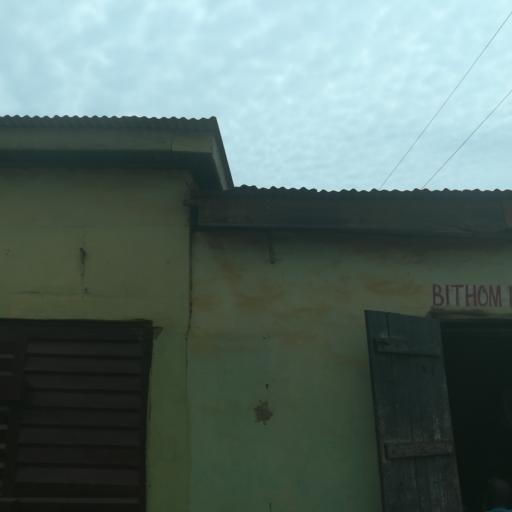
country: NG
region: Lagos
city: Ejirin
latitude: 6.6479
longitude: 3.7131
